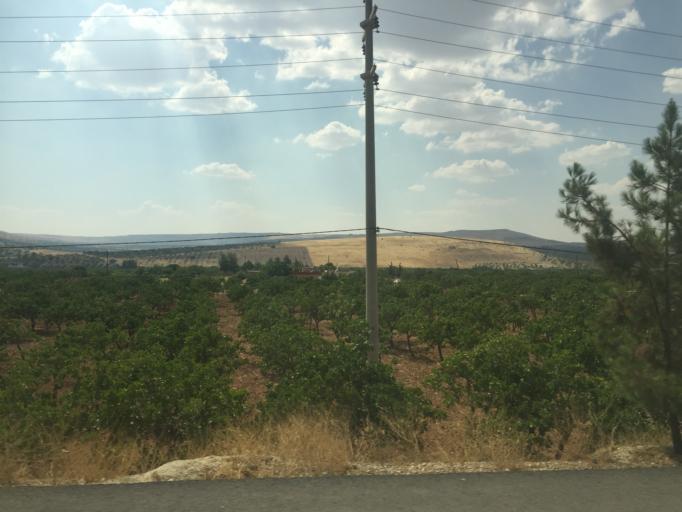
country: TR
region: Sanliurfa
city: Sanliurfa
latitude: 37.2403
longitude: 38.7939
